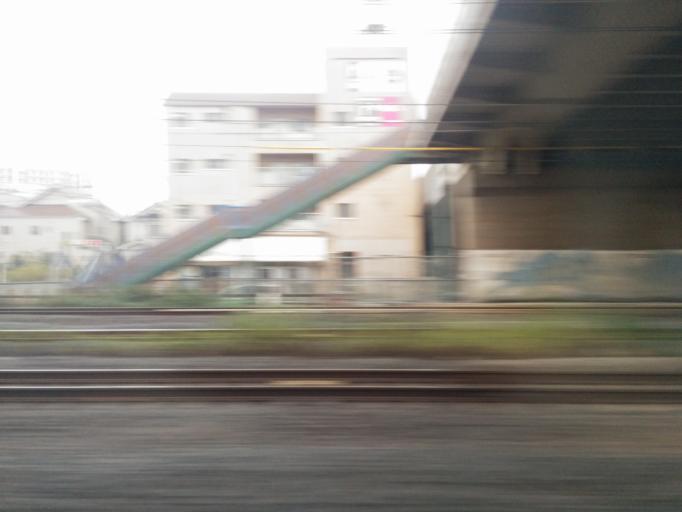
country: JP
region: Chiba
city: Funabashi
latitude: 35.7038
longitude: 139.9676
